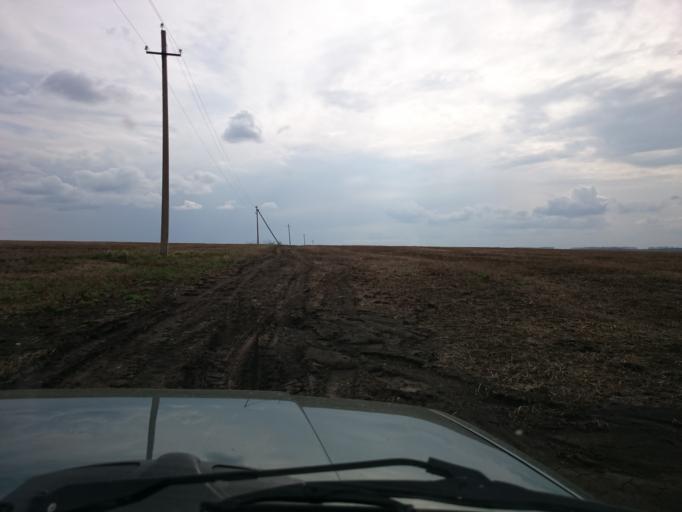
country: RU
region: Mordoviya
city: Kadoshkino
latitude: 54.0236
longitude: 44.4743
